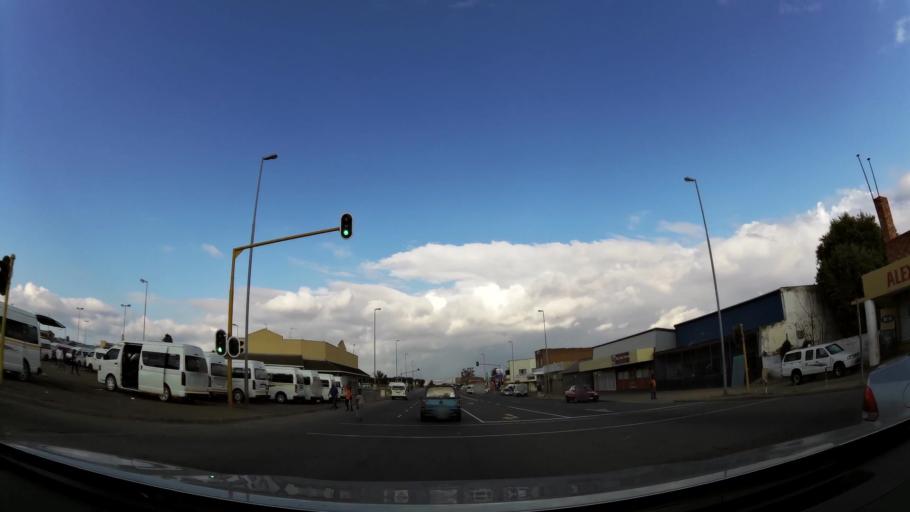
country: ZA
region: Eastern Cape
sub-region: Nelson Mandela Bay Metropolitan Municipality
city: Uitenhage
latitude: -33.7723
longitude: 25.4003
